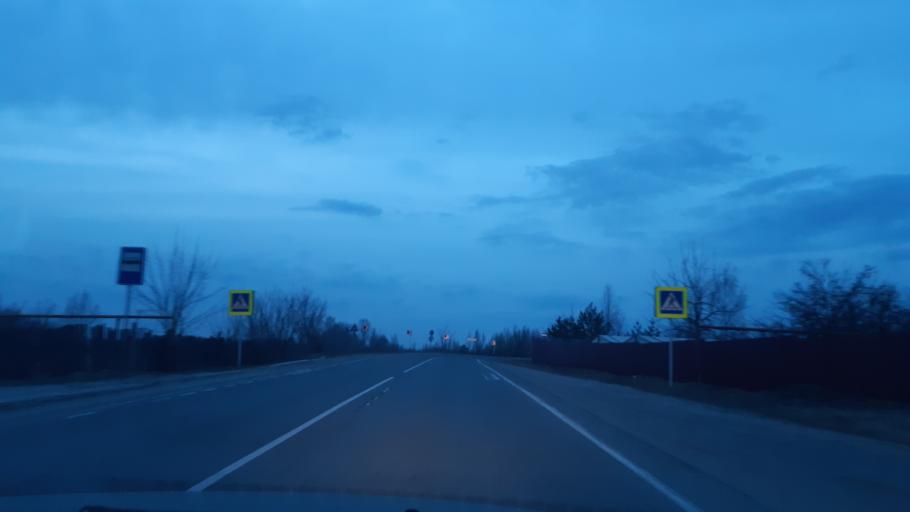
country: RU
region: Vladimir
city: Luknovo
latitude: 56.2144
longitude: 42.0303
